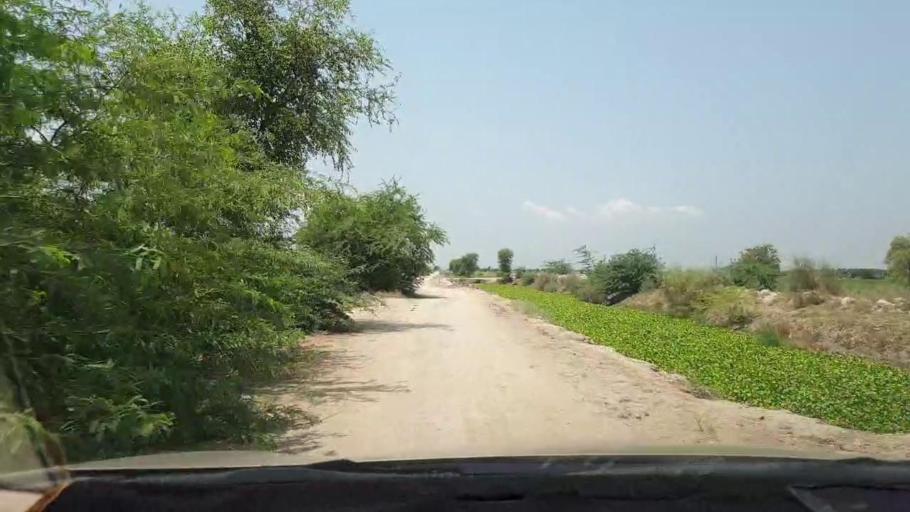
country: PK
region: Sindh
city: Naudero
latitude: 27.6625
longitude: 68.2678
